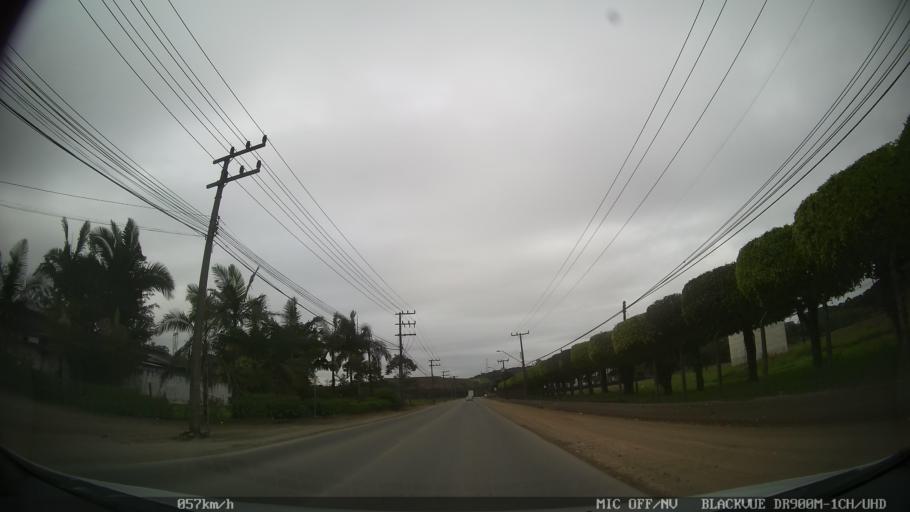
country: BR
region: Santa Catarina
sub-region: Joinville
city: Joinville
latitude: -26.2339
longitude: -48.8966
